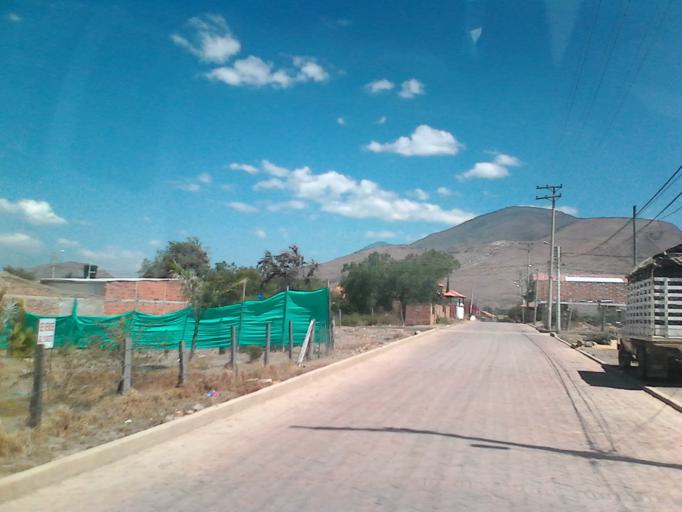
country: CO
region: Boyaca
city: Sachica
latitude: 5.5816
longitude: -73.5442
